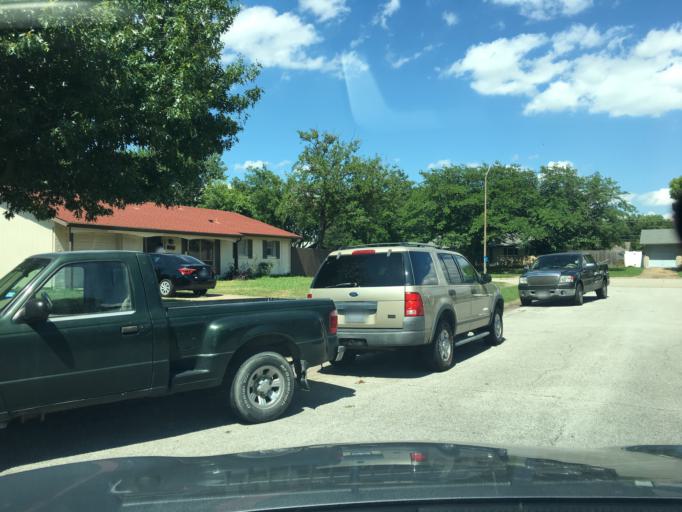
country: US
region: Texas
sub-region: Dallas County
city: Richardson
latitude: 32.9522
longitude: -96.7147
